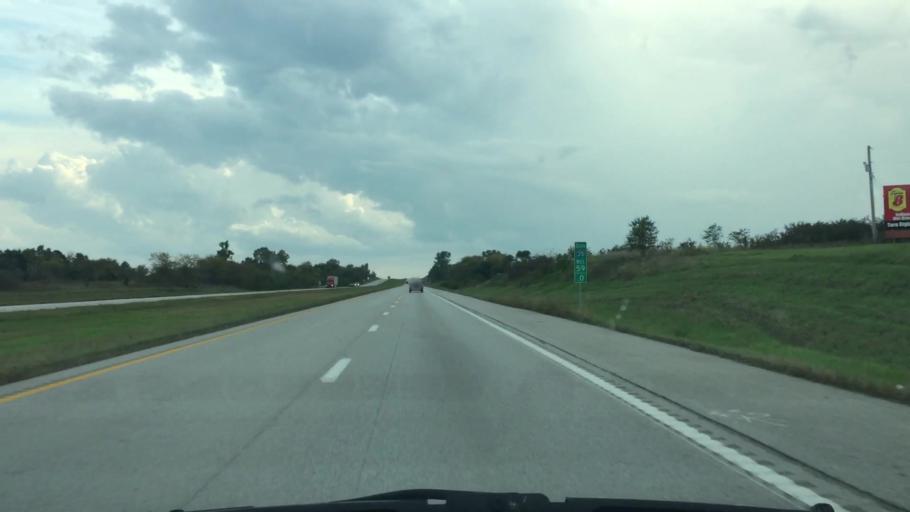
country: US
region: Missouri
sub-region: Clinton County
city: Cameron
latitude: 39.8195
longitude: -94.1921
